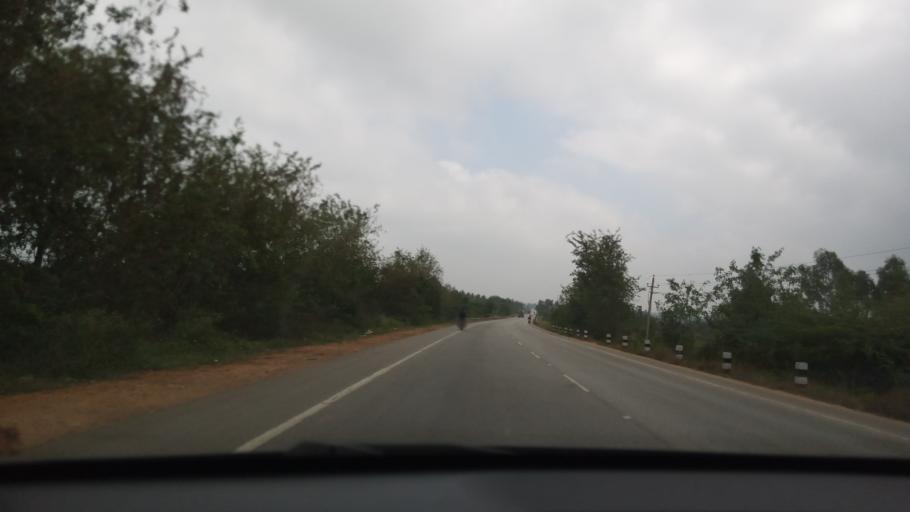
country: IN
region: Karnataka
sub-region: Chikkaballapur
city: Chintamani
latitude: 13.3625
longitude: 78.0443
